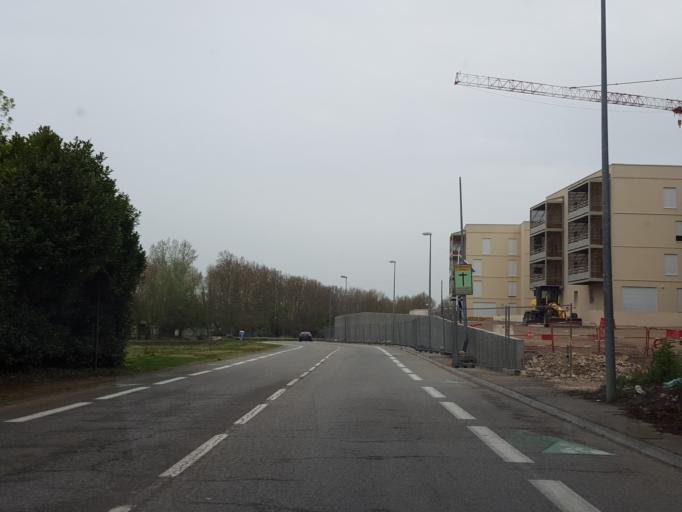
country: FR
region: Provence-Alpes-Cote d'Azur
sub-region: Departement du Vaucluse
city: Montfavet
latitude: 43.9173
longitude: 4.8824
